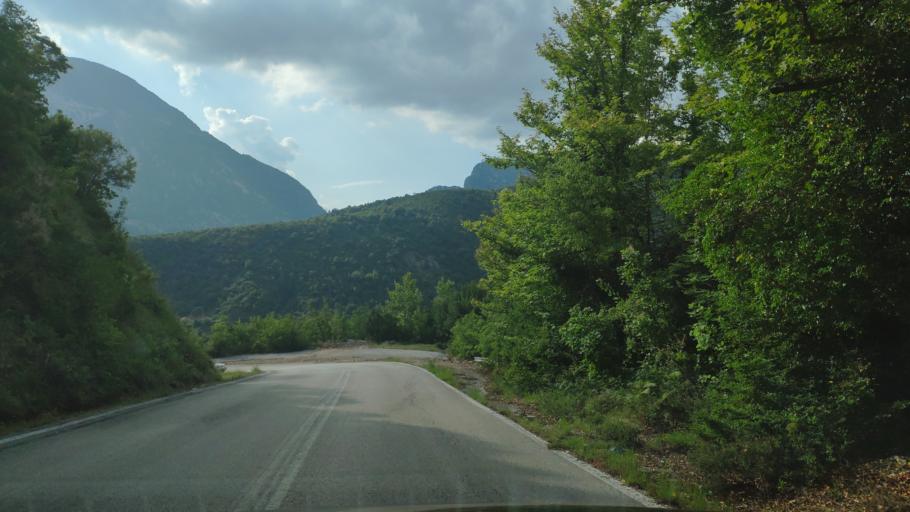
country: GR
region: Epirus
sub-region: Nomos Artas
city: Agios Dimitrios
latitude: 39.4597
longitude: 21.0391
